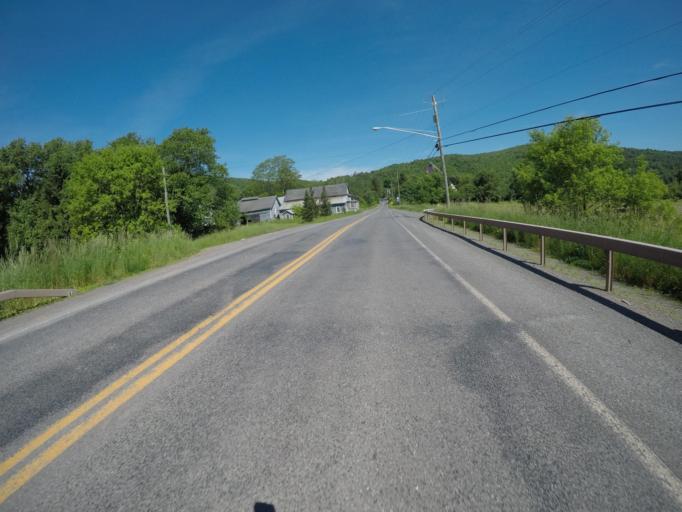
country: US
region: New York
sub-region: Delaware County
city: Delhi
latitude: 42.2088
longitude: -74.9768
